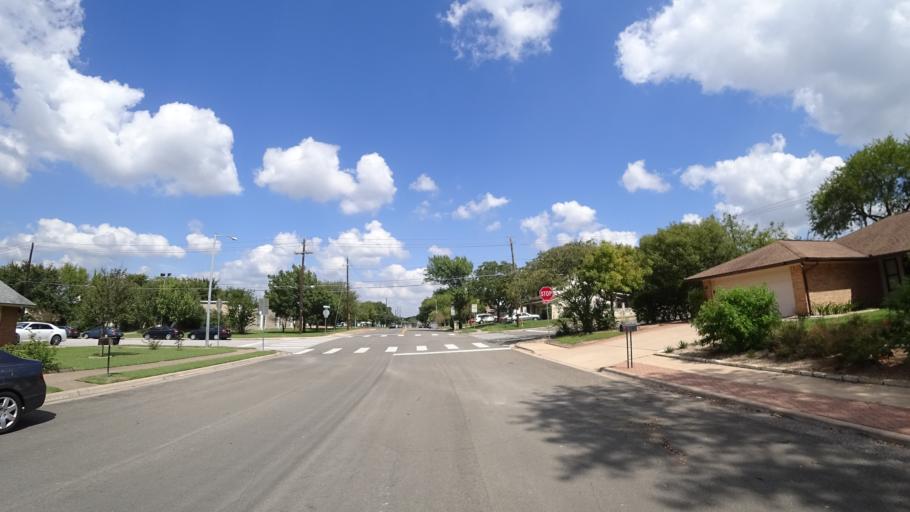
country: US
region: Texas
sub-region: Travis County
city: Onion Creek
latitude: 30.1929
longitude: -97.7868
